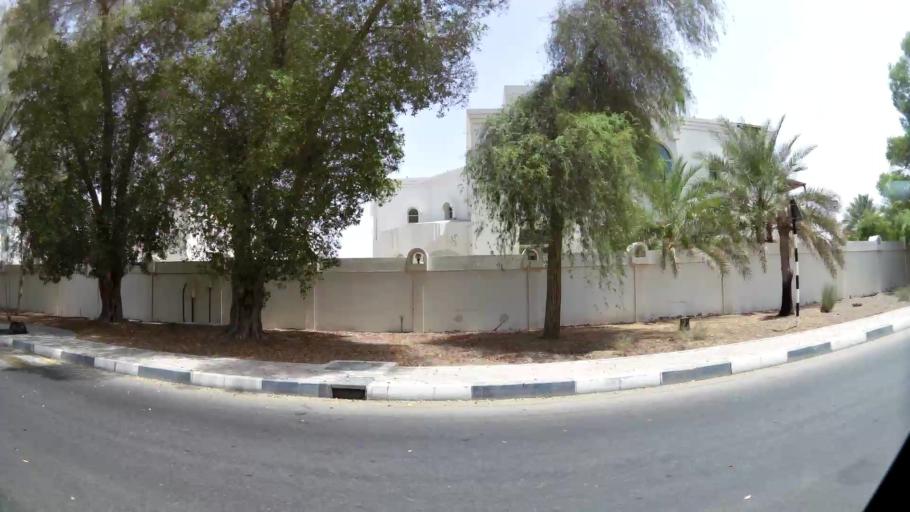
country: AE
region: Abu Dhabi
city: Al Ain
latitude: 24.1975
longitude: 55.7388
